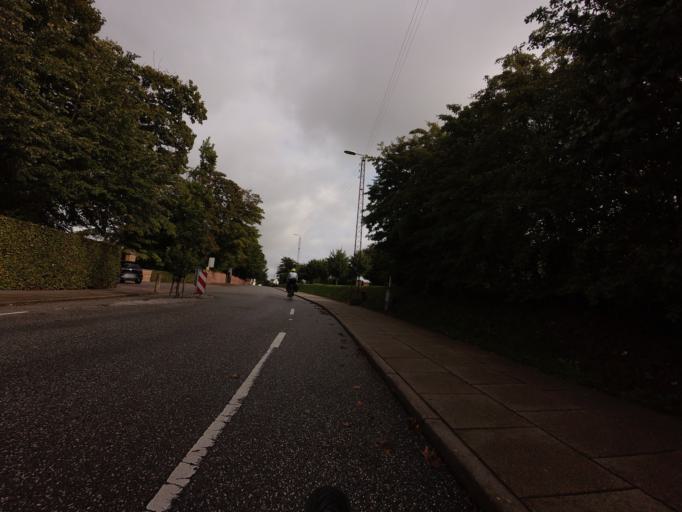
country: DK
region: North Denmark
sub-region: Hjorring Kommune
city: Hjorring
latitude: 57.4632
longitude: 9.9804
